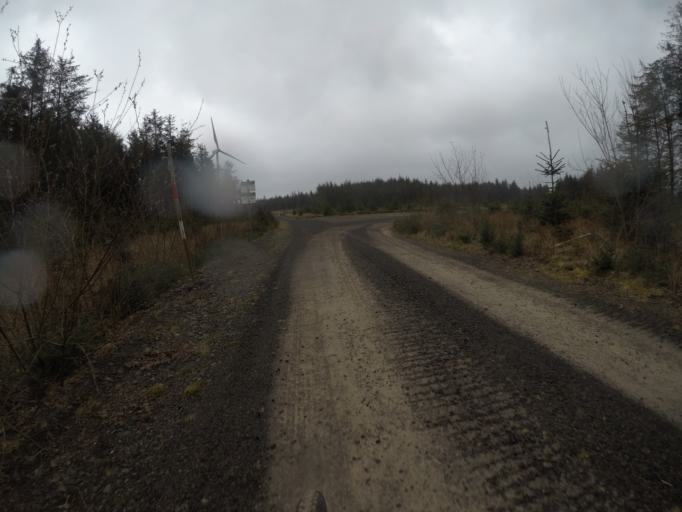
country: GB
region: Scotland
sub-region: East Ayrshire
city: Newmilns
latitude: 55.6404
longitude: -4.3201
